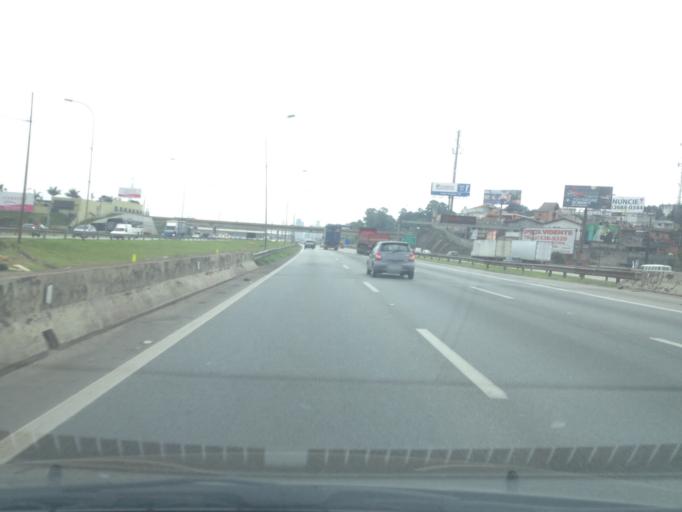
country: BR
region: Sao Paulo
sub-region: Osasco
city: Osasco
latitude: -23.5106
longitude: -46.8084
